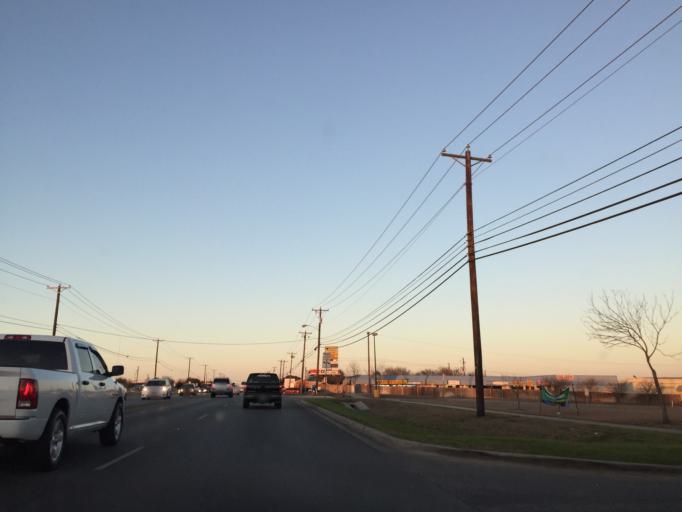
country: US
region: Texas
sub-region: Travis County
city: Pflugerville
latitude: 30.4381
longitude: -97.6128
